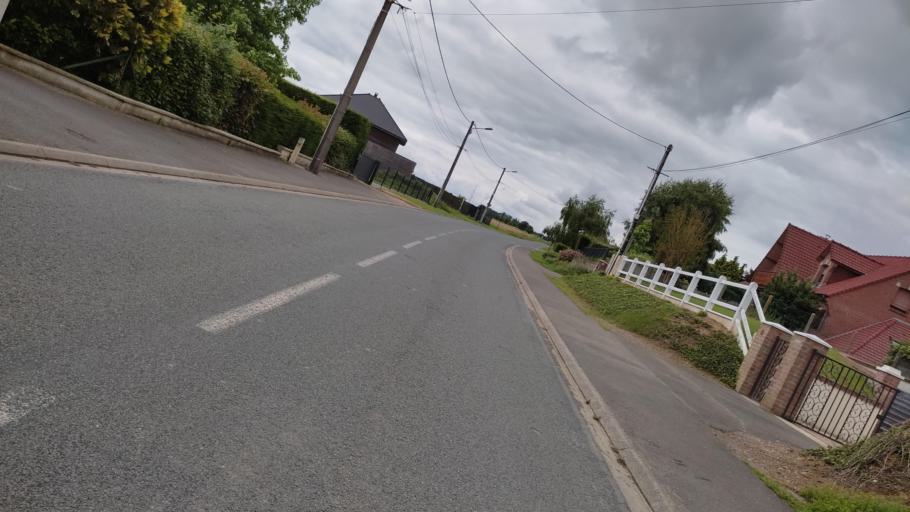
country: FR
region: Nord-Pas-de-Calais
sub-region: Departement du Pas-de-Calais
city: Beaumetz-les-Loges
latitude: 50.2642
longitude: 2.6669
